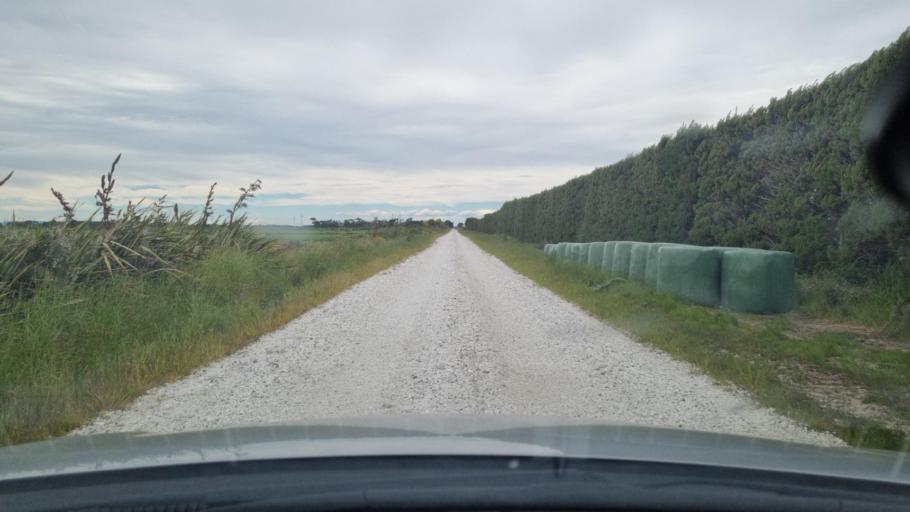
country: NZ
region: Southland
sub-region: Invercargill City
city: Invercargill
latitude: -46.4992
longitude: 168.4123
